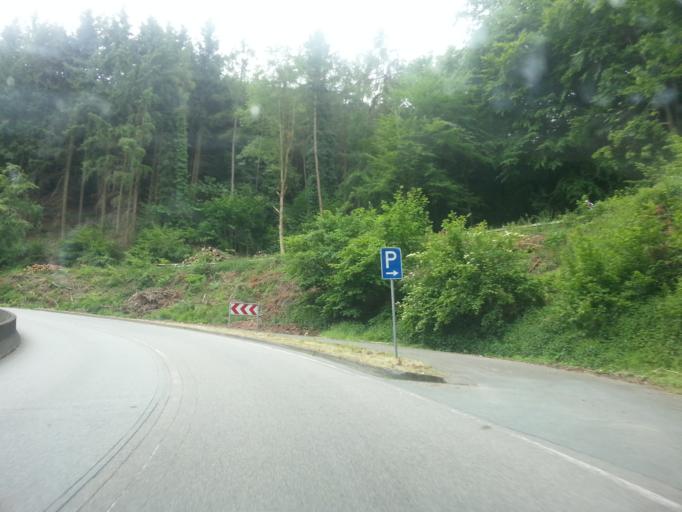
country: DE
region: Hesse
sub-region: Regierungsbezirk Darmstadt
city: Seeheim-Jugenheim
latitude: 49.7498
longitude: 8.6445
